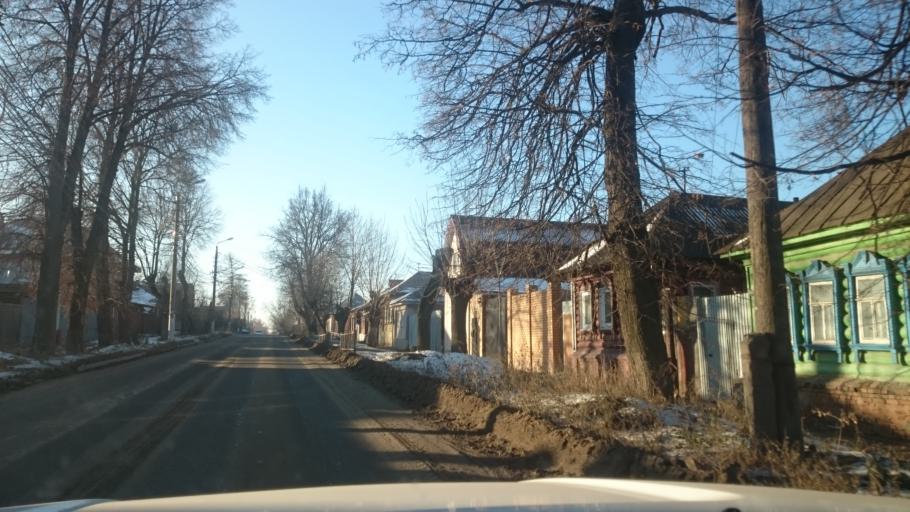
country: RU
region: Tula
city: Tula
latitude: 54.2060
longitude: 37.6392
